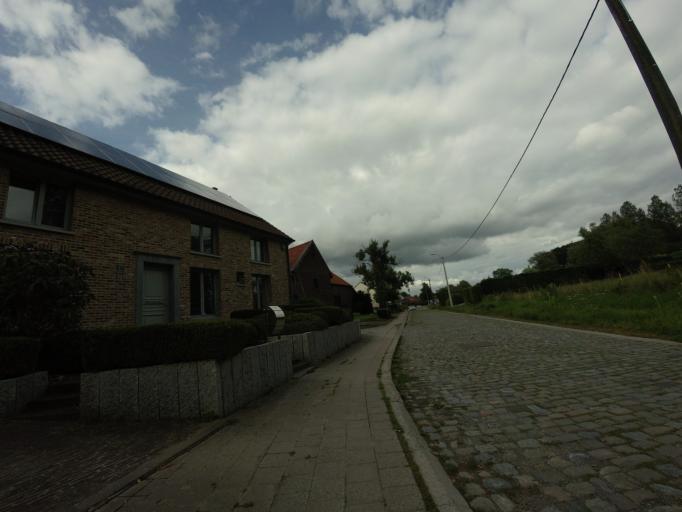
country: BE
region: Flanders
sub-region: Provincie Vlaams-Brabant
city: Grimbergen
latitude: 50.9334
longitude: 4.3541
